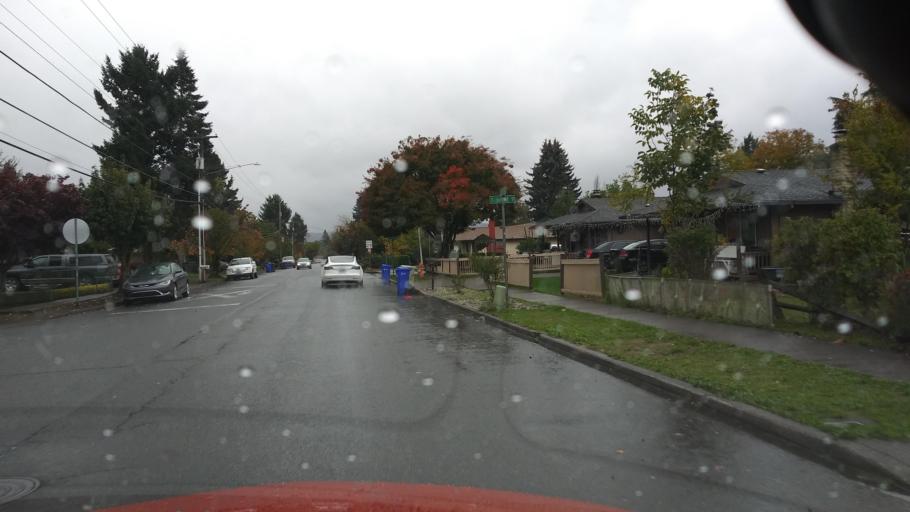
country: US
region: Oregon
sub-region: Washington County
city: Cornelius
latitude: 45.5193
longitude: -123.0668
